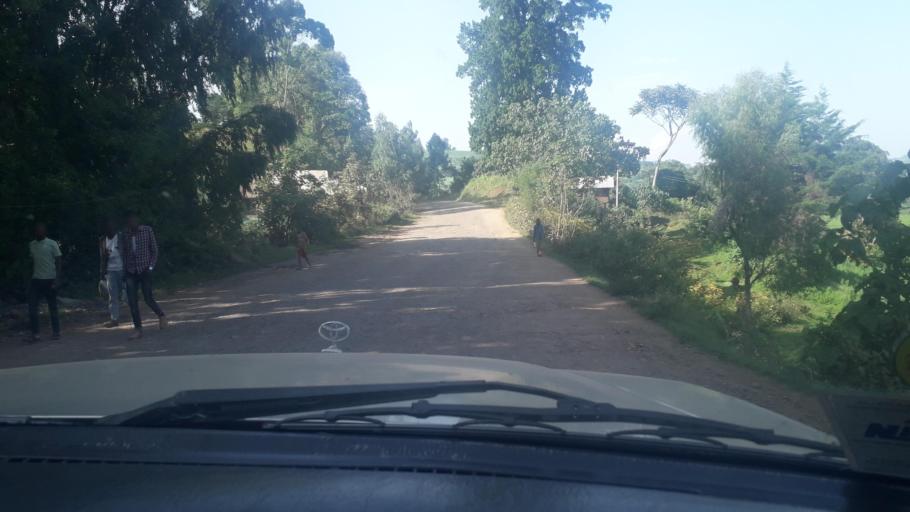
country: ET
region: Oromiya
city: Jima
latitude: 7.3806
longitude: 36.8688
